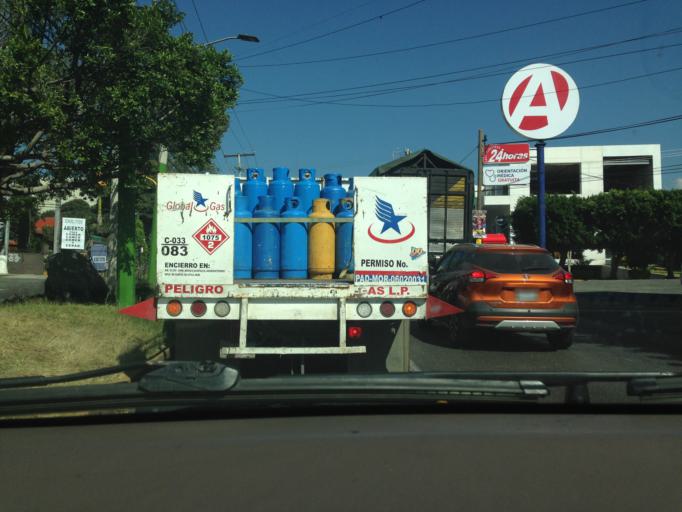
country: MX
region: Morelos
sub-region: Cuernavaca
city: Fraccionamiento Lomas de Ahuatlan
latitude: 18.9498
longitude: -99.2350
